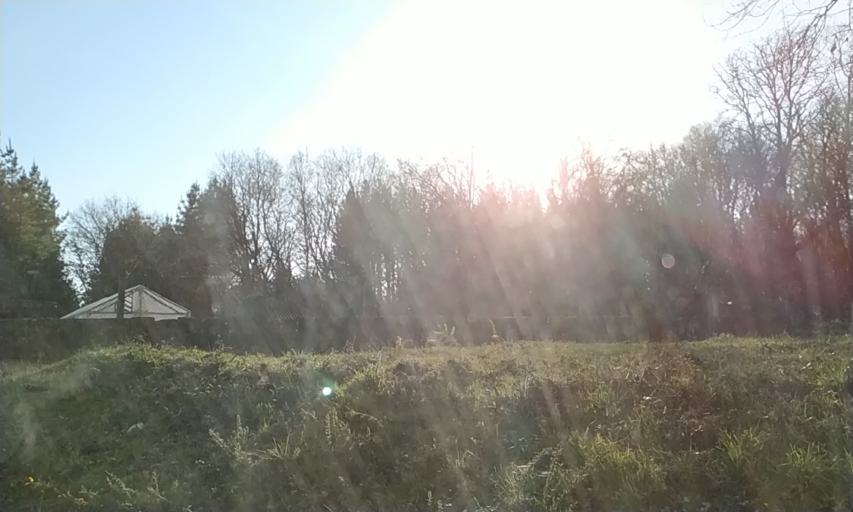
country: ES
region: Galicia
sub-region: Provincia de Lugo
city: Corgo
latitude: 42.9347
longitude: -7.4471
